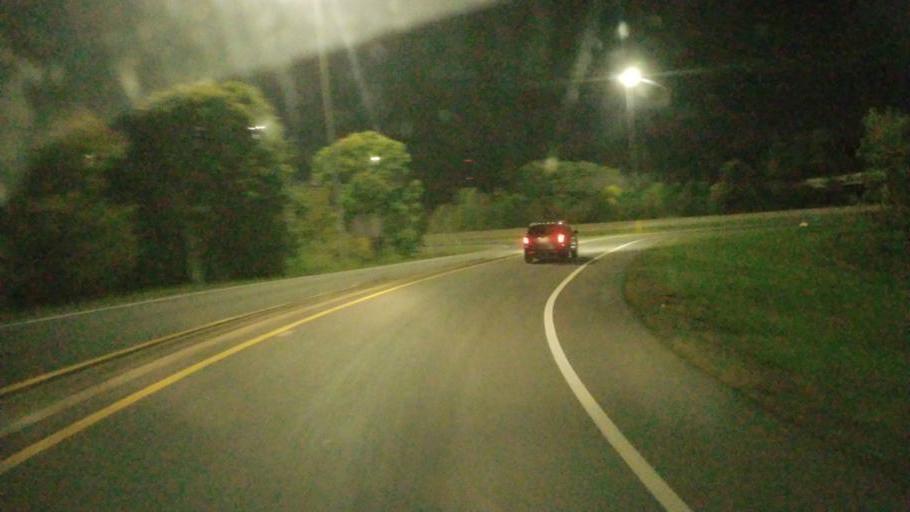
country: US
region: Ohio
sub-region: Wayne County
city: Wooster
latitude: 40.7915
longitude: -81.9345
